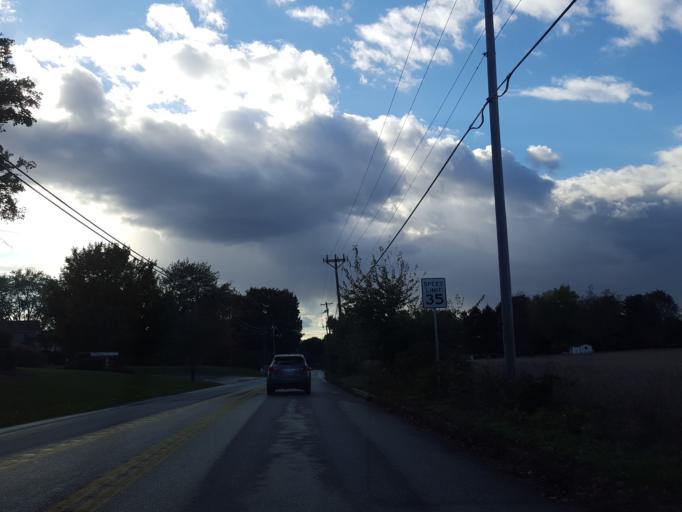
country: US
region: Pennsylvania
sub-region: York County
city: Spry
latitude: 39.9308
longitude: -76.6629
